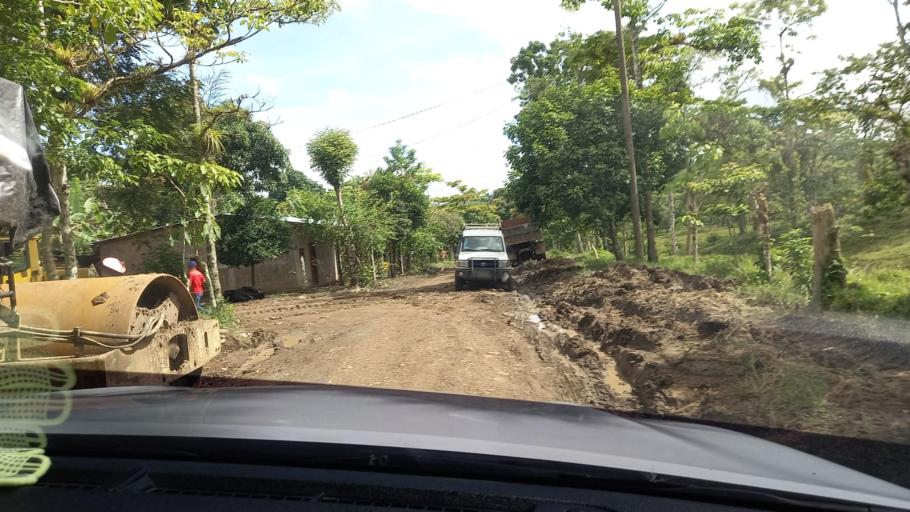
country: NI
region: Jinotega
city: San Jose de Bocay
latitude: 13.3817
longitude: -85.6848
